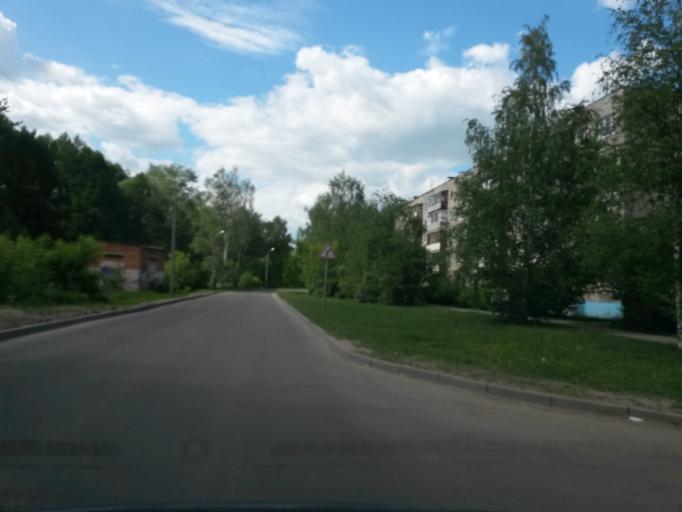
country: RU
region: Jaroslavl
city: Yaroslavl
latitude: 57.6442
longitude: 39.9421
